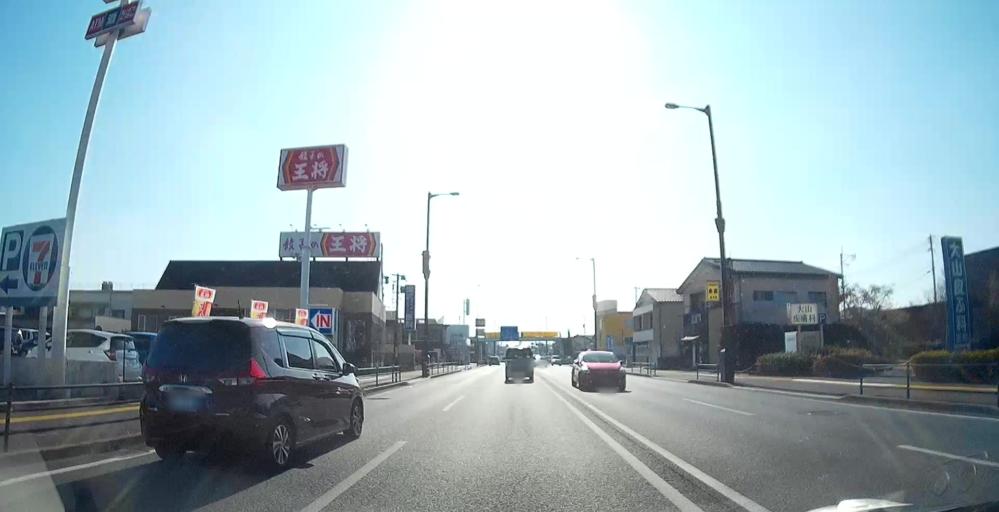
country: JP
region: Kumamoto
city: Kumamoto
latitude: 32.7671
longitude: 130.6918
